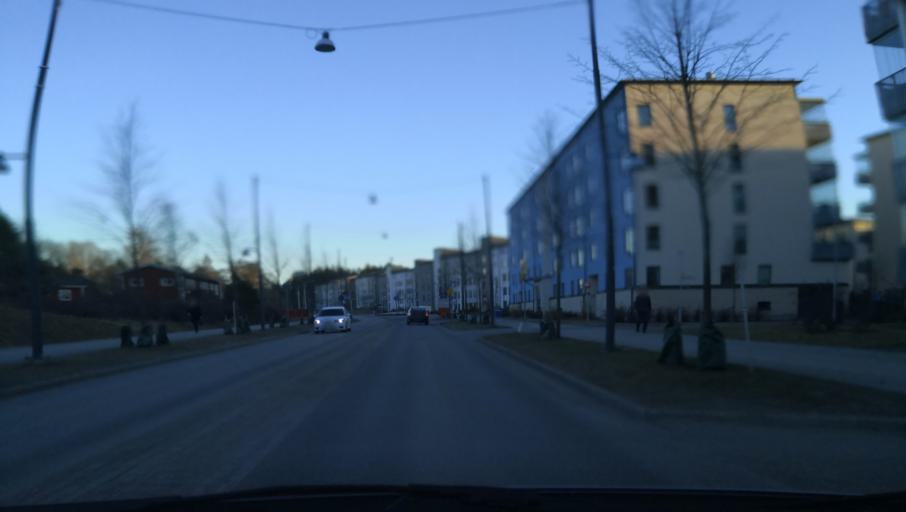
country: SE
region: Stockholm
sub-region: Varmdo Kommun
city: Gustavsberg
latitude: 59.3207
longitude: 18.3874
